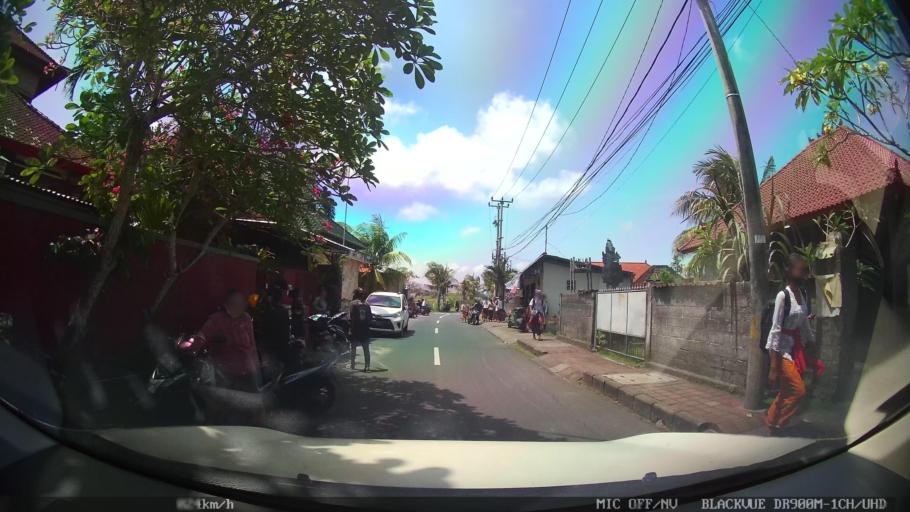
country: ID
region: Bali
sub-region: Kabupaten Gianyar
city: Ubud
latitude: -8.5608
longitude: 115.3182
